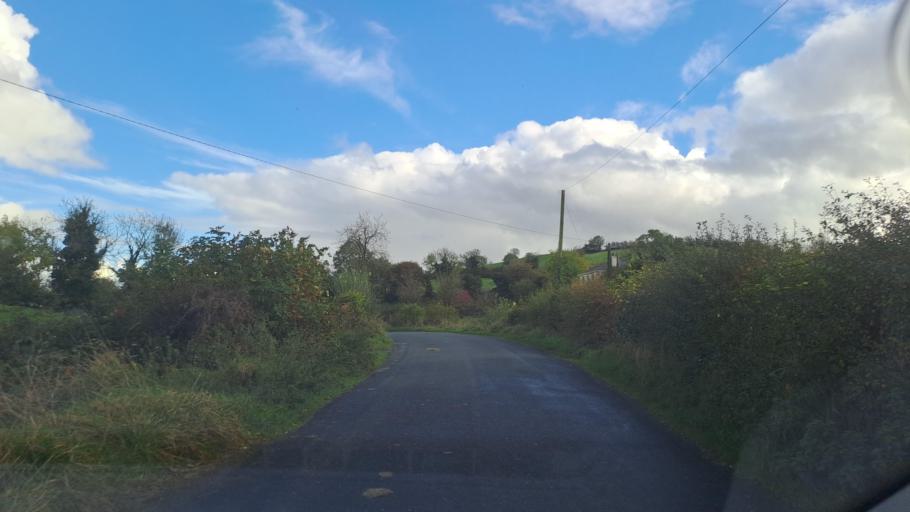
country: IE
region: Ulster
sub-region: An Cabhan
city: Bailieborough
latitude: 53.9937
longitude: -6.9766
